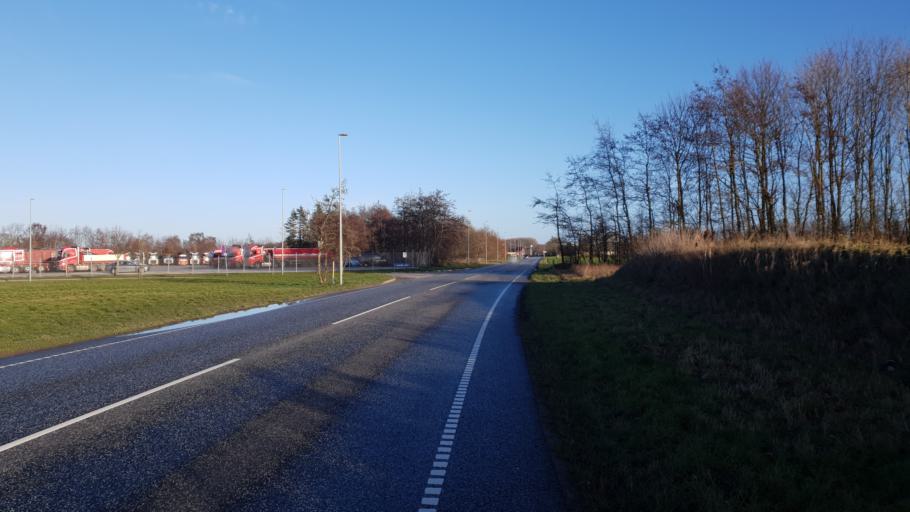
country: DK
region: Central Jutland
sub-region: Hedensted Kommune
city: Hedensted
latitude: 55.8044
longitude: 9.6816
